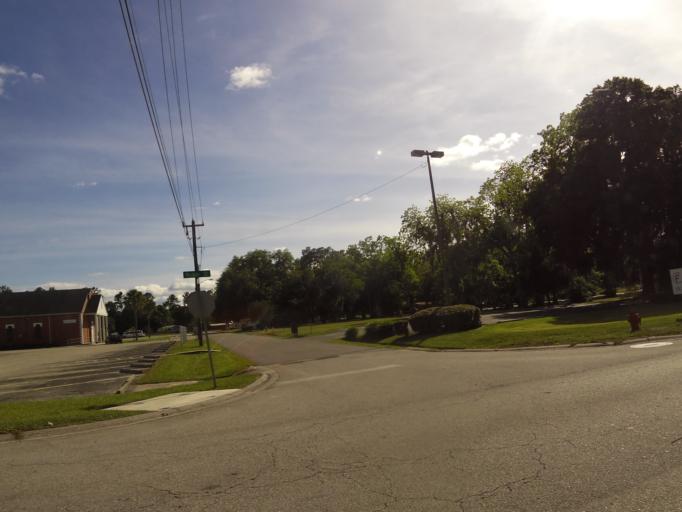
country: US
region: Florida
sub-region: Nassau County
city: Callahan
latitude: 30.5612
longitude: -81.8336
